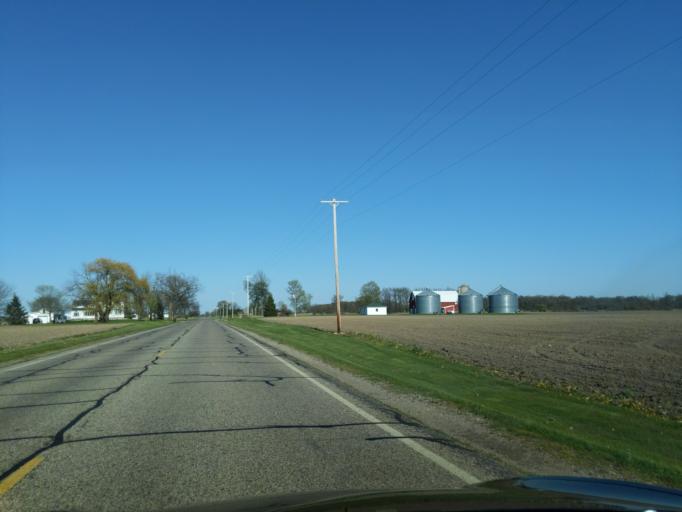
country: US
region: Michigan
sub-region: Ionia County
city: Ionia
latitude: 42.8858
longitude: -85.0194
